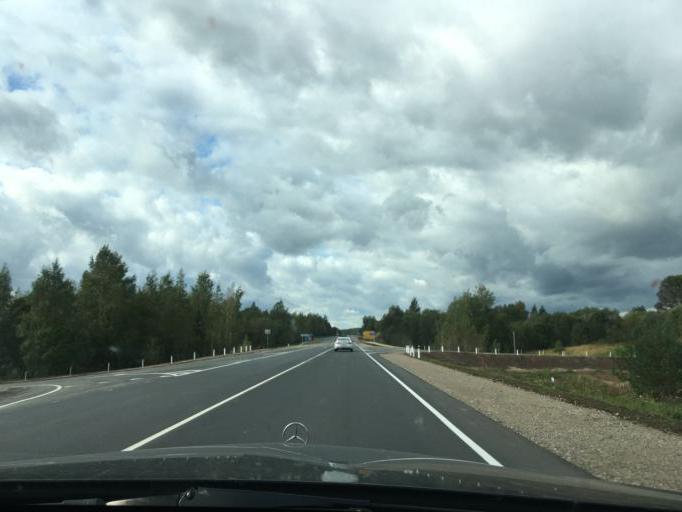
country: RU
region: Tverskaya
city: Toropets
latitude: 56.3285
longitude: 31.2166
